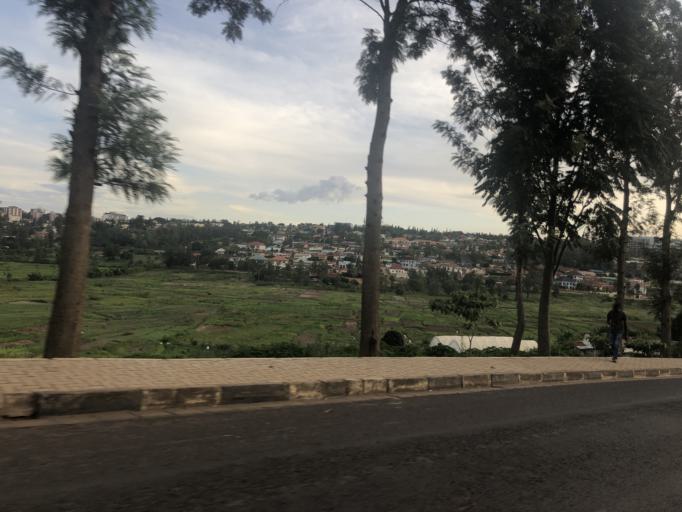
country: RW
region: Kigali
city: Kigali
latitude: -1.9314
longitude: 30.0910
